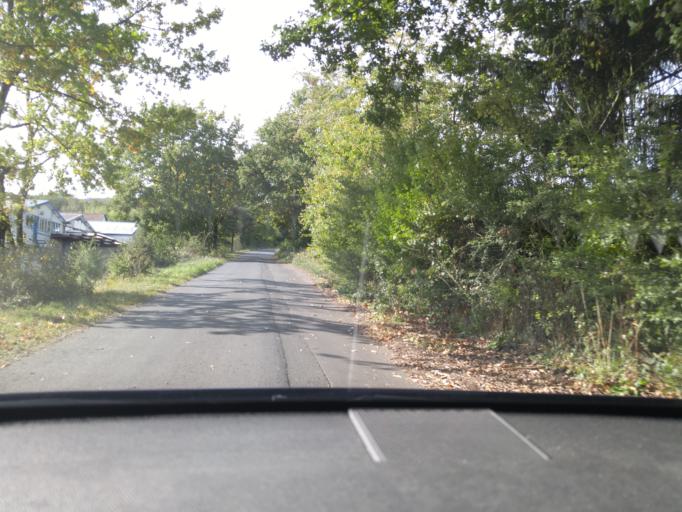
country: DE
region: Hesse
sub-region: Regierungsbezirk Darmstadt
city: Rosbach vor der Hohe
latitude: 50.3321
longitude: 8.6989
